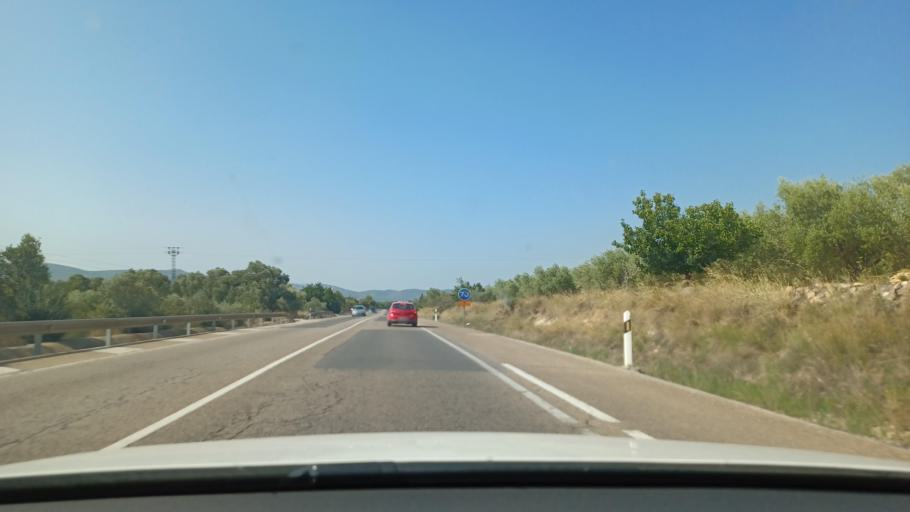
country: ES
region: Valencia
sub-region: Provincia de Castello
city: Alcala de Xivert
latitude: 40.2854
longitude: 0.2249
